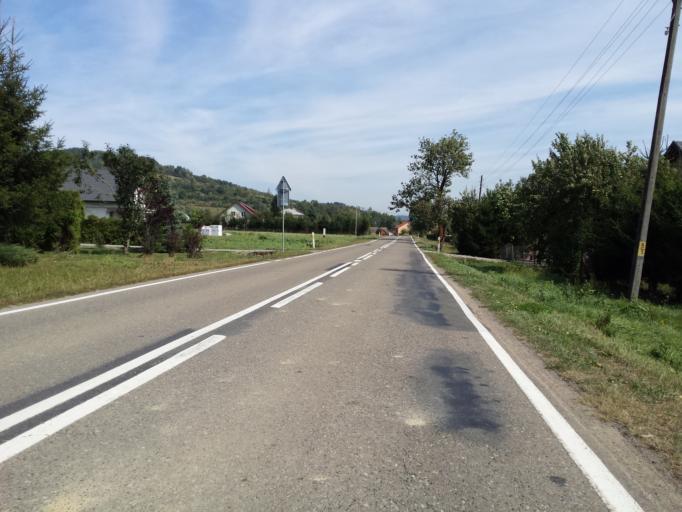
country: PL
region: Subcarpathian Voivodeship
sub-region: Powiat leski
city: Baligrod
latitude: 49.4005
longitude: 22.2857
